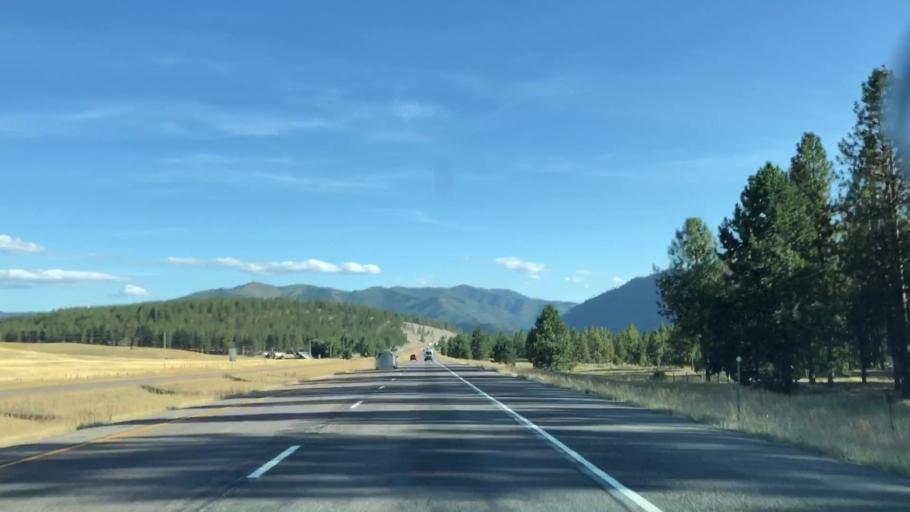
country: US
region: Montana
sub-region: Mineral County
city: Superior
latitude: 47.0349
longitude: -114.7450
